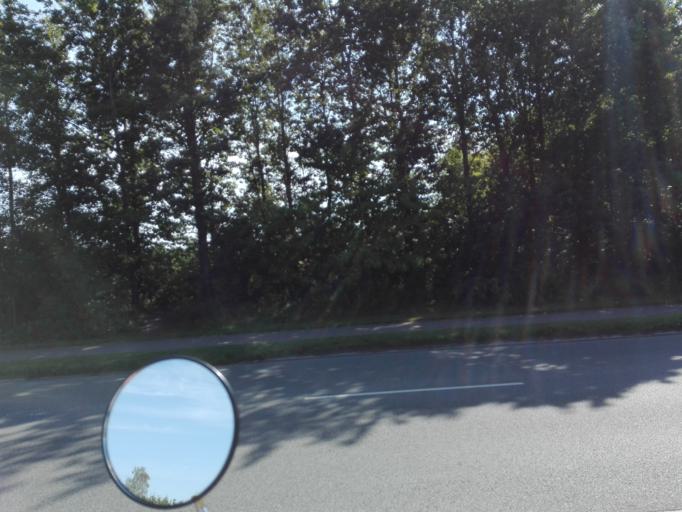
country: DK
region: Central Jutland
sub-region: Arhus Kommune
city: Tranbjerg
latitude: 56.0943
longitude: 10.1287
